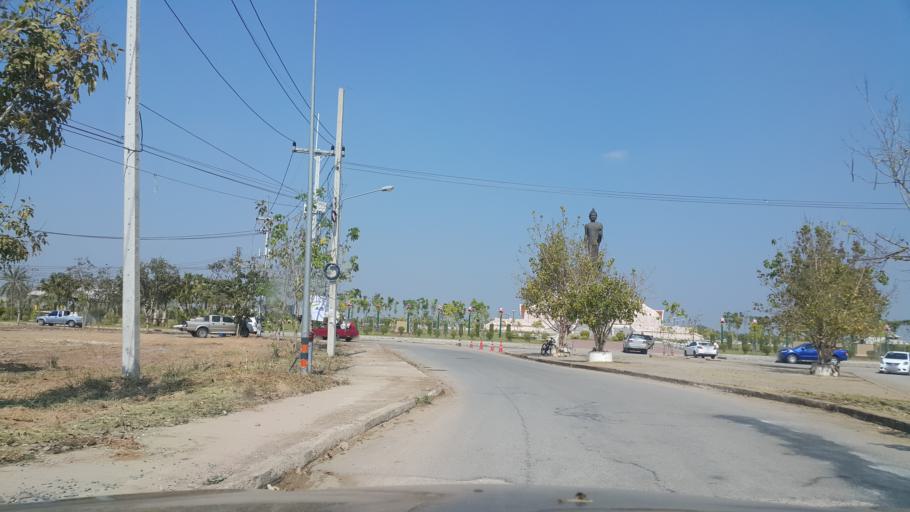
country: TH
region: Khon Kaen
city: Khon Kaen
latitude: 16.5101
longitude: 102.8684
